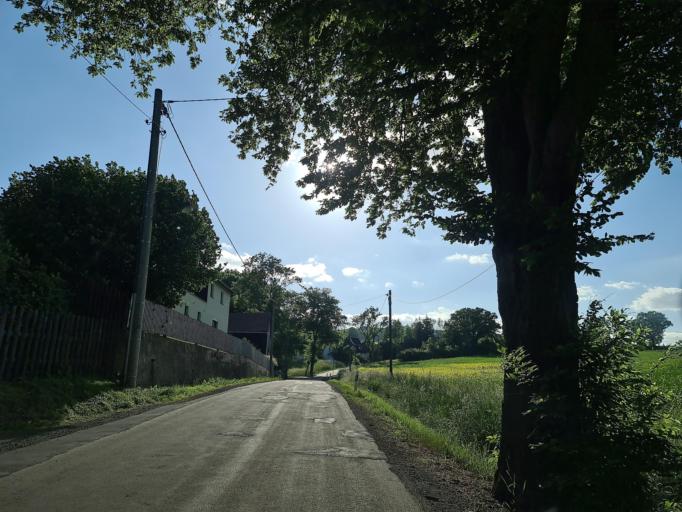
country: DE
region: Saxony
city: Weischlitz
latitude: 50.4910
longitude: 12.0405
